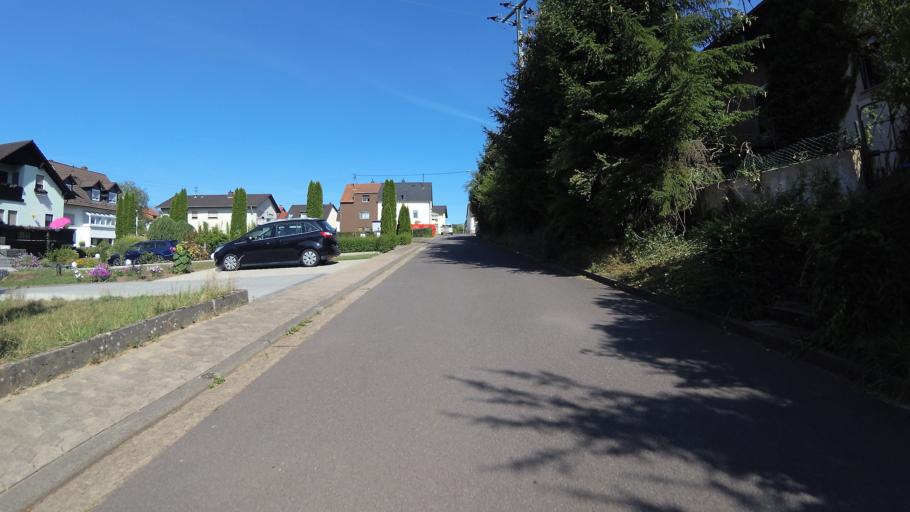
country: DE
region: Saarland
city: Eppelborn
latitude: 49.3646
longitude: 6.9823
